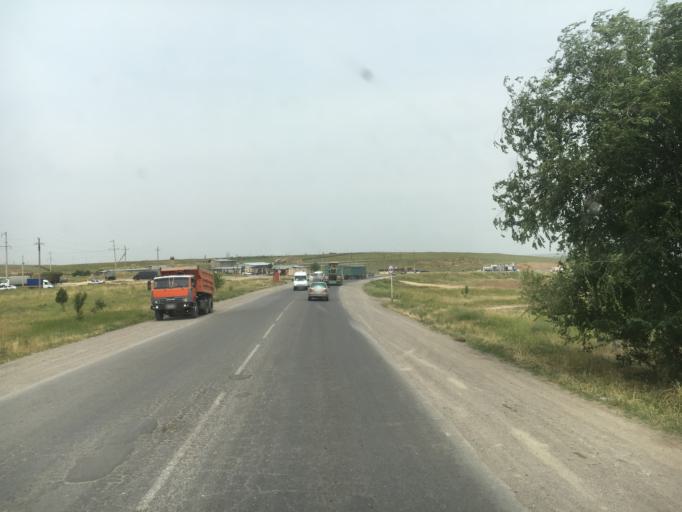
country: KZ
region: Ongtustik Qazaqstan
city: Shymkent
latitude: 42.3227
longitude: 69.5165
